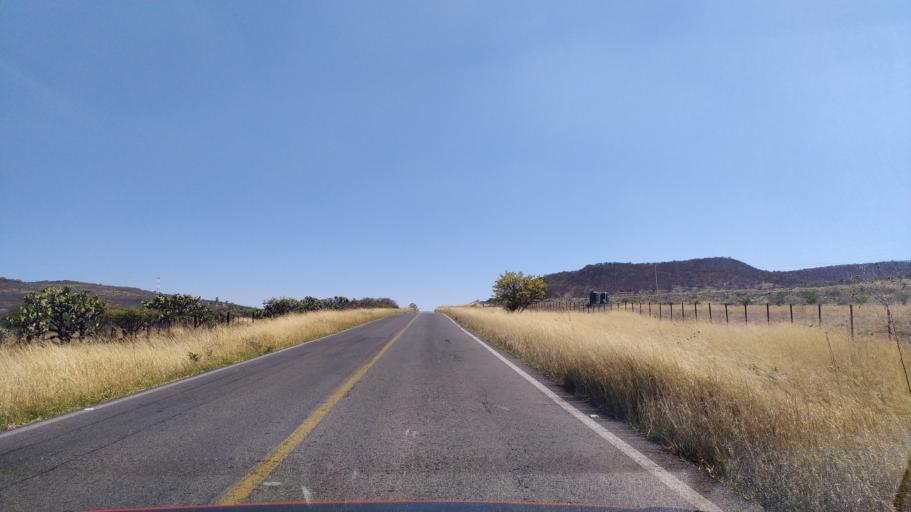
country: MX
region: Guanajuato
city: Ciudad Manuel Doblado
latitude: 20.5732
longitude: -101.9706
